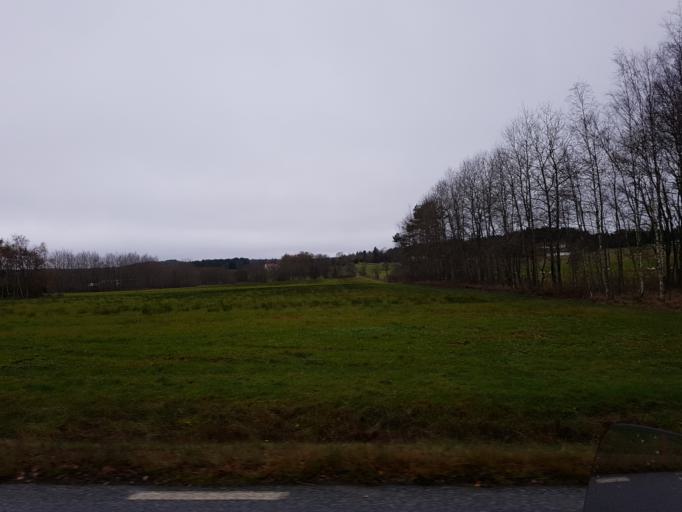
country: SE
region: Vaestra Goetaland
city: Svanesund
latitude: 58.1667
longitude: 11.7870
